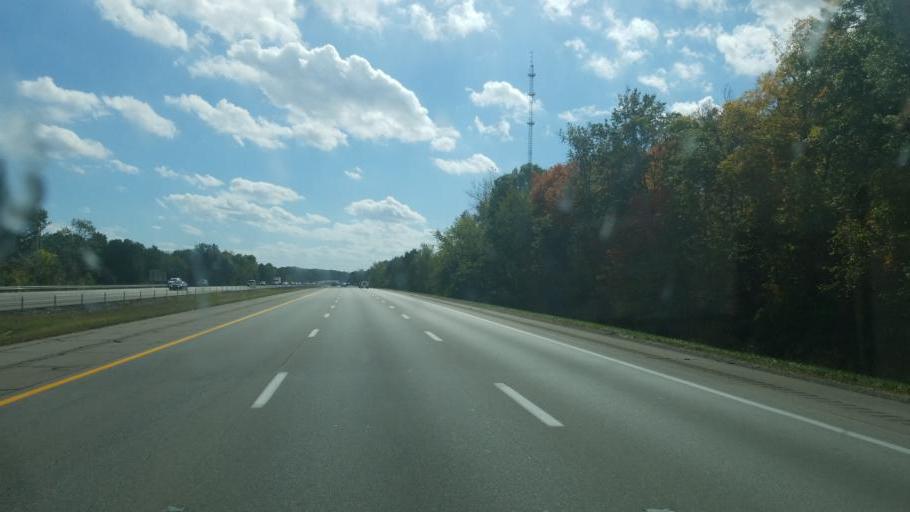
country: US
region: Ohio
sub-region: Delaware County
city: Sunbury
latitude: 40.2488
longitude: -82.9292
